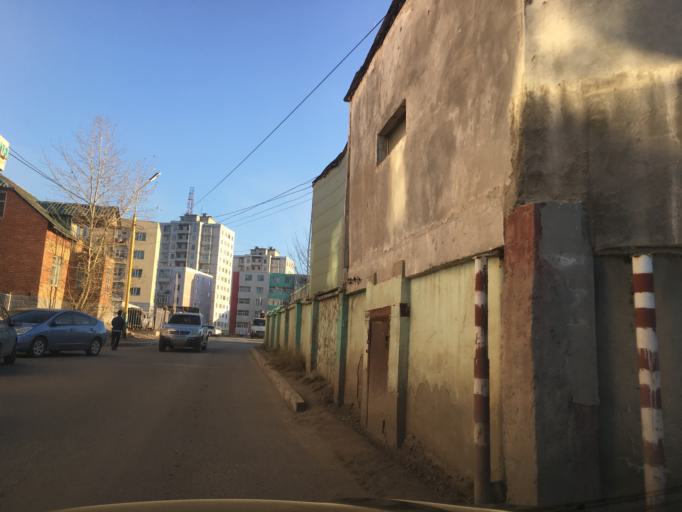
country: MN
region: Ulaanbaatar
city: Ulaanbaatar
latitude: 47.9278
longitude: 106.8861
